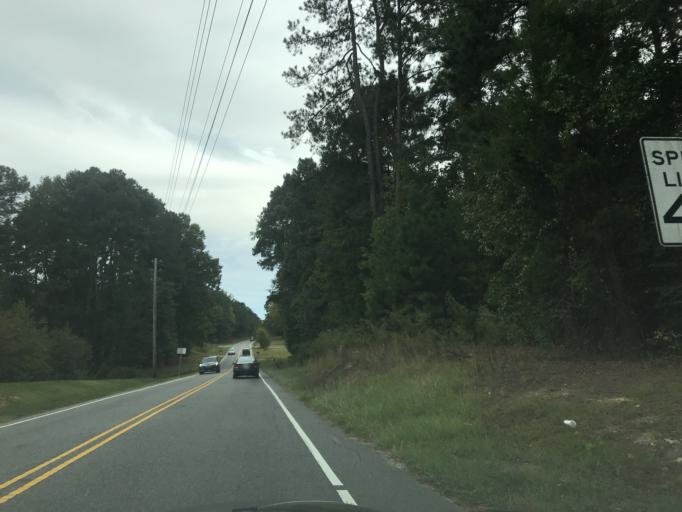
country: US
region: North Carolina
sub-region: Wake County
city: Rolesville
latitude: 35.9085
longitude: -78.5049
